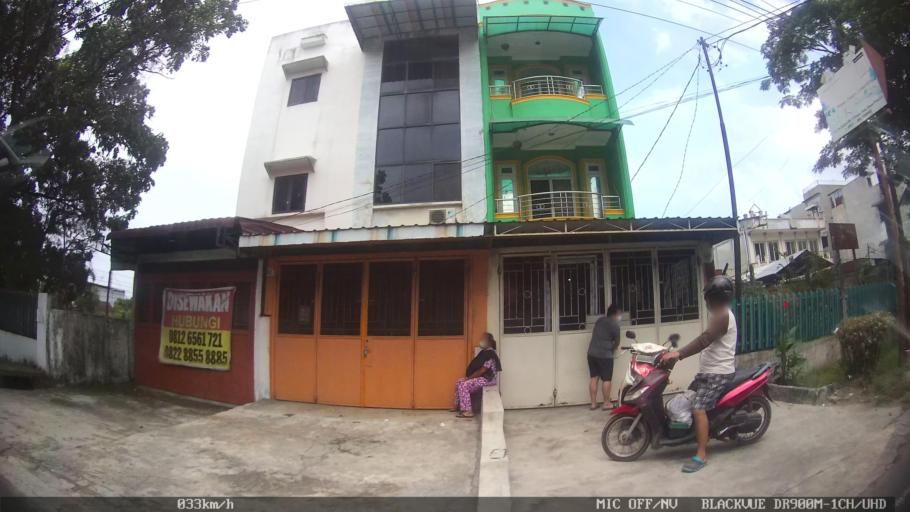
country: ID
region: North Sumatra
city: Medan
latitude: 3.6349
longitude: 98.6686
